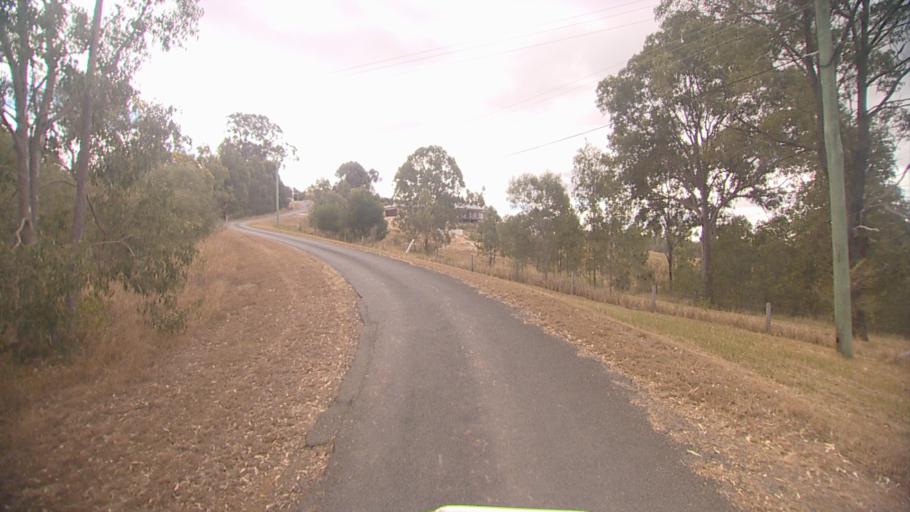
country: AU
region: Queensland
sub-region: Logan
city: Cedar Vale
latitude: -27.9024
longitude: 153.0388
